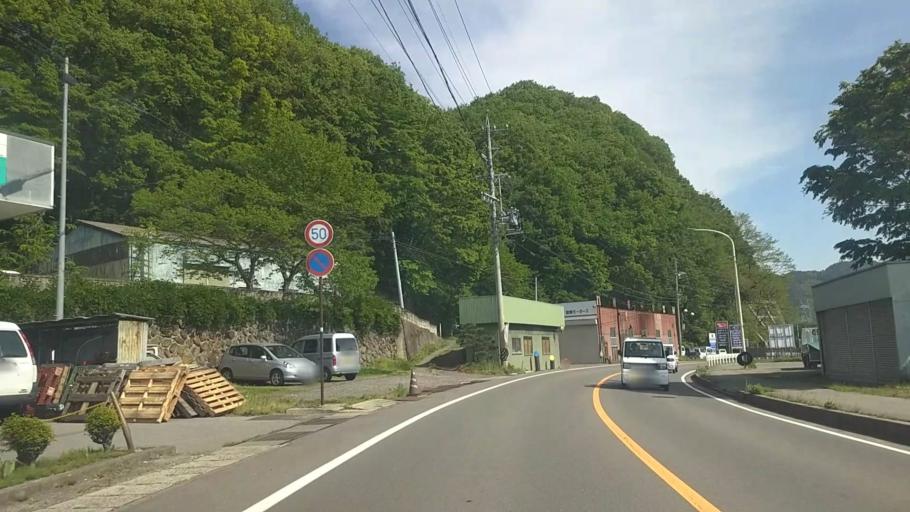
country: JP
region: Nagano
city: Saku
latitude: 36.0971
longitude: 138.4823
